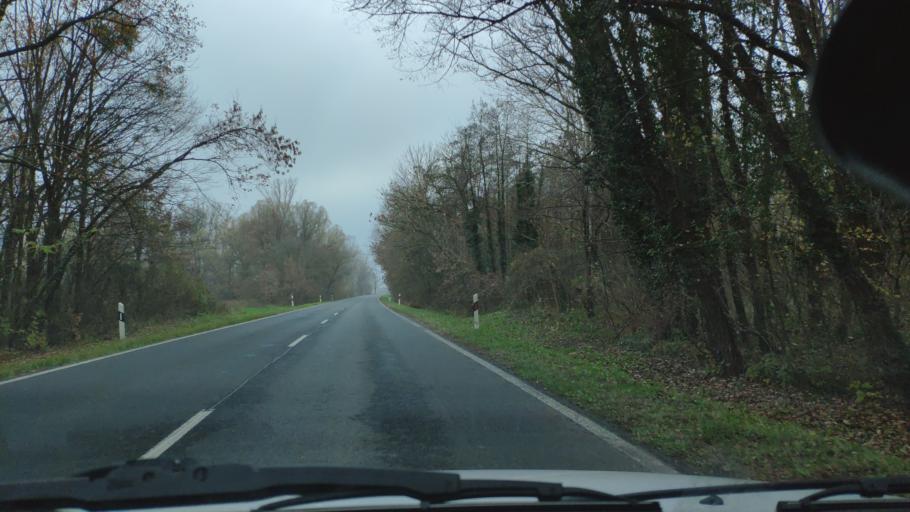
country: HU
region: Somogy
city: Balatonbereny
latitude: 46.6252
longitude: 17.2870
